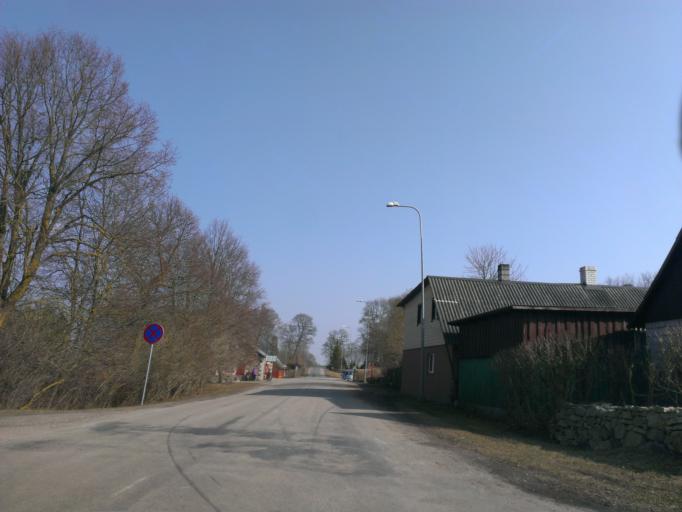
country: EE
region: Saare
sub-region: Orissaare vald
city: Orissaare
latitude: 58.5040
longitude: 23.1163
